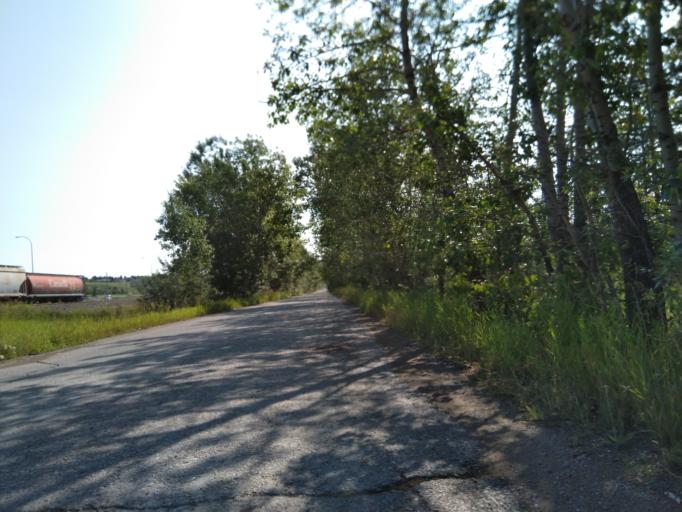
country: CA
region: Alberta
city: Calgary
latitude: 51.1020
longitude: -114.2253
